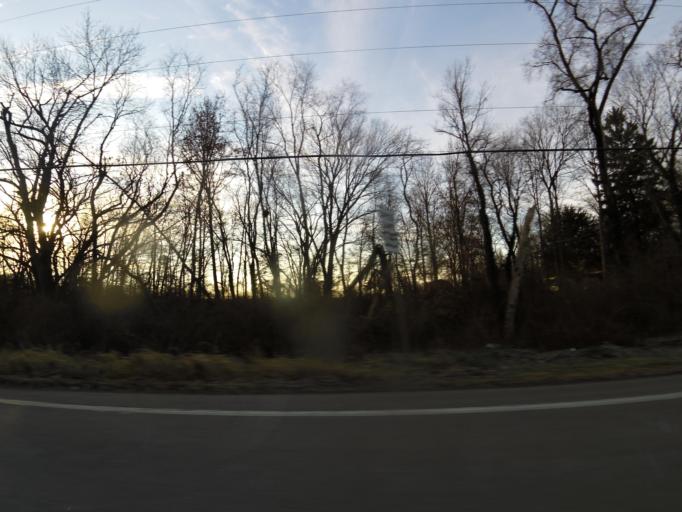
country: US
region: Illinois
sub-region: Fayette County
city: Vandalia
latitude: 38.9576
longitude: -89.1136
